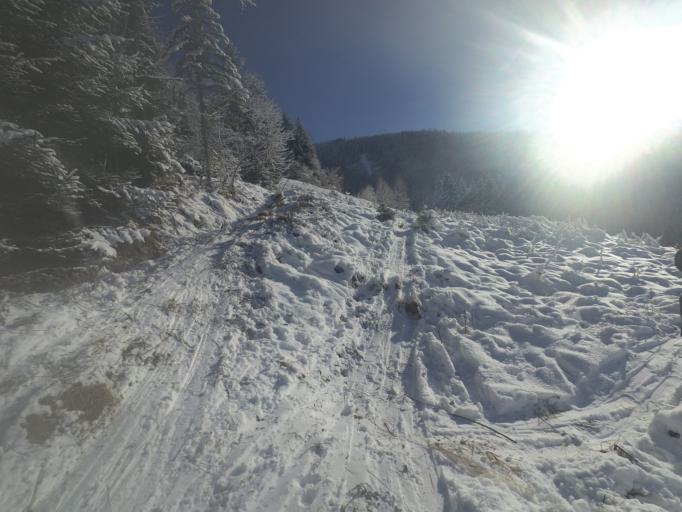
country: AT
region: Salzburg
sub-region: Politischer Bezirk Sankt Johann im Pongau
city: Sankt Johann im Pongau
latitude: 47.3186
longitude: 13.2064
